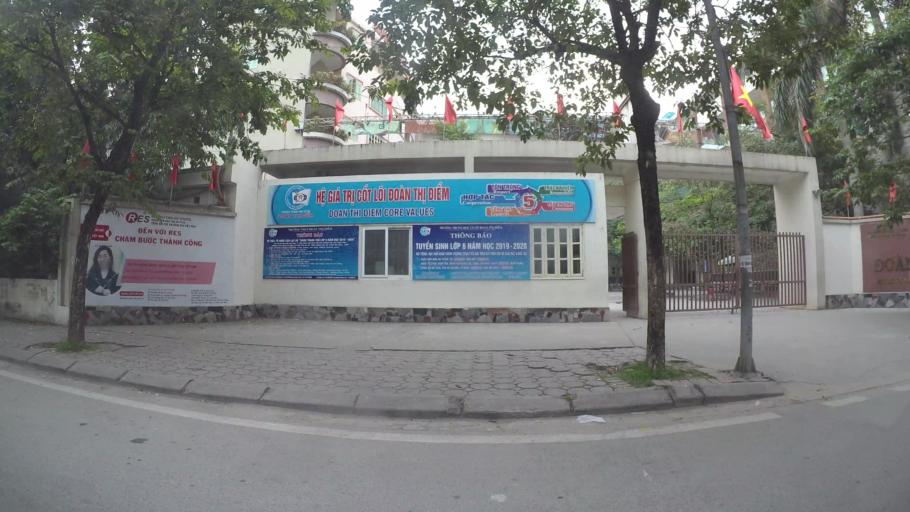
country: VN
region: Ha Noi
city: Cau Dien
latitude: 21.0333
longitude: 105.7642
